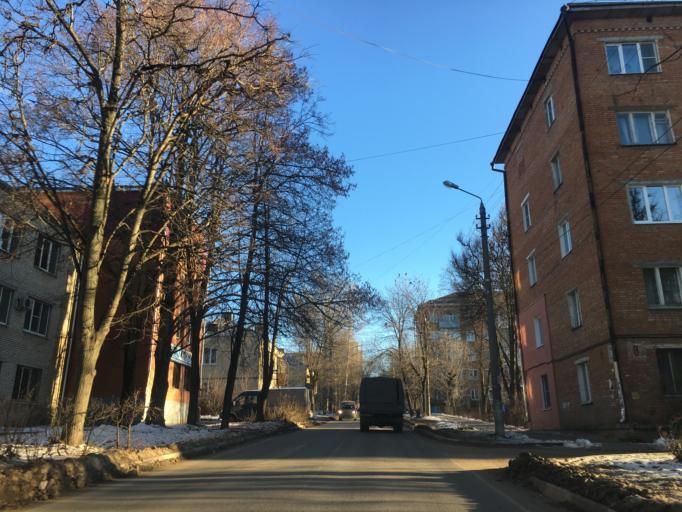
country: RU
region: Tula
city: Mendeleyevskiy
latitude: 54.1660
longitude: 37.5763
